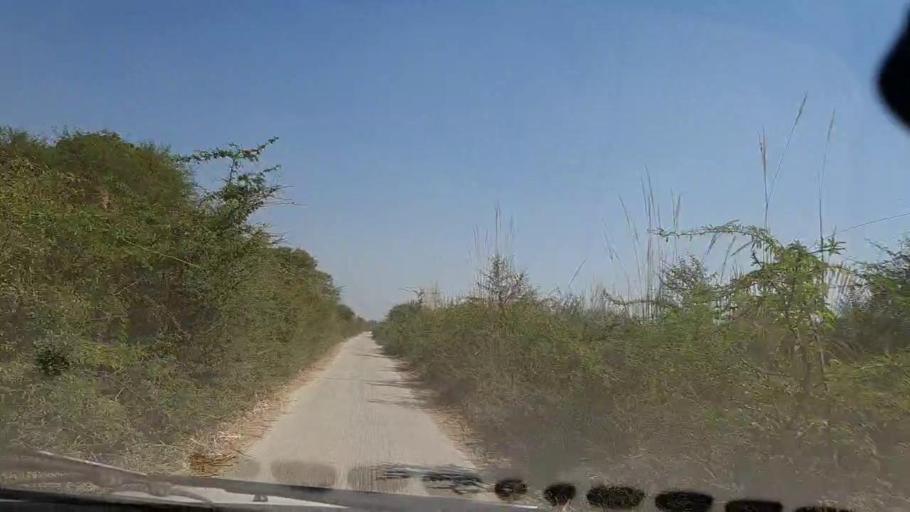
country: PK
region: Sindh
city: Mirpur Khas
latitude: 25.4718
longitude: 69.0414
